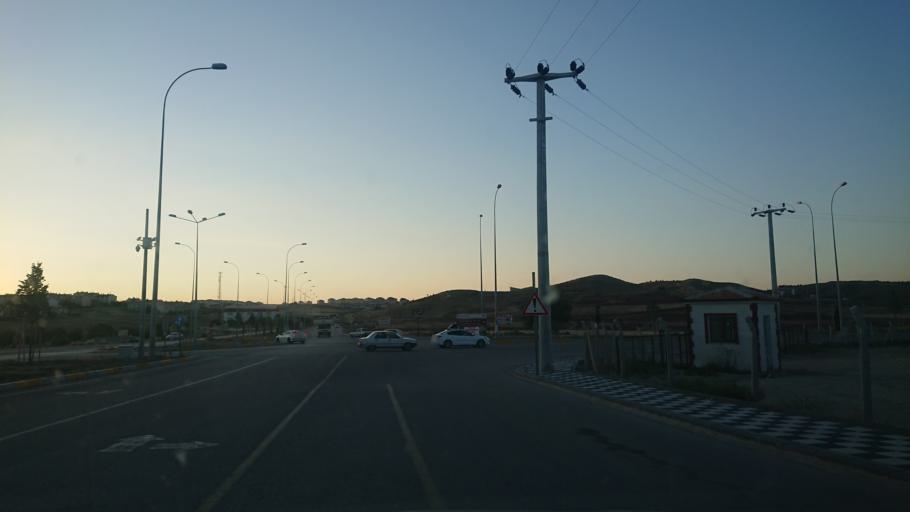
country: TR
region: Aksaray
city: Aksaray
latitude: 38.4100
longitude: 34.0116
